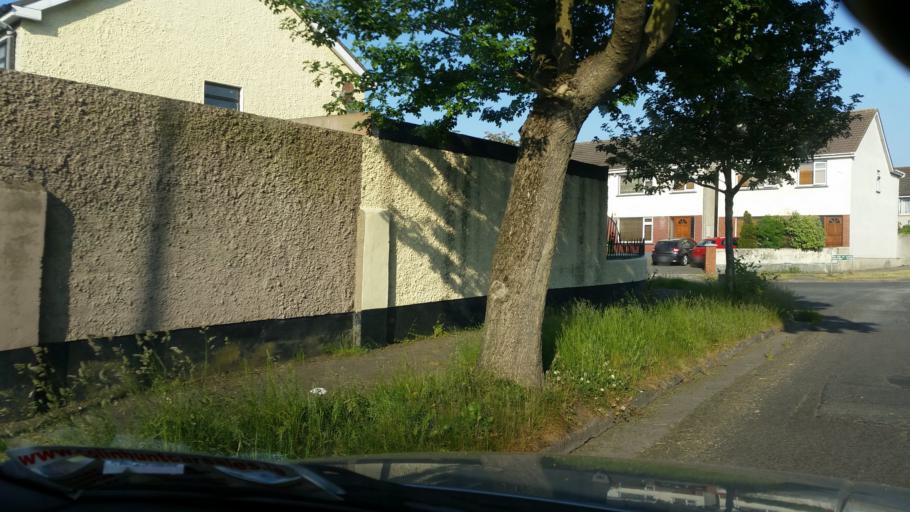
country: IE
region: Leinster
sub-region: Fingal County
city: Blanchardstown
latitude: 53.4009
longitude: -6.3709
